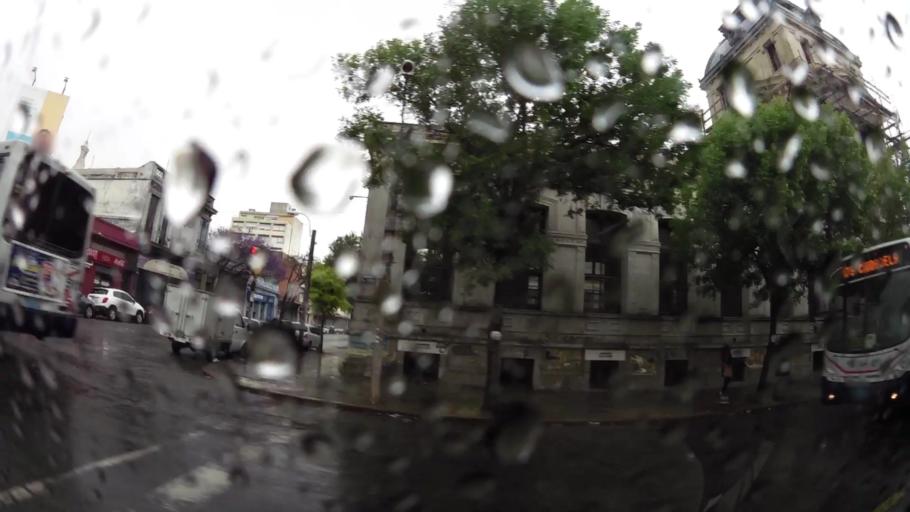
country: UY
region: Montevideo
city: Montevideo
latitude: -34.8887
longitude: -56.1862
